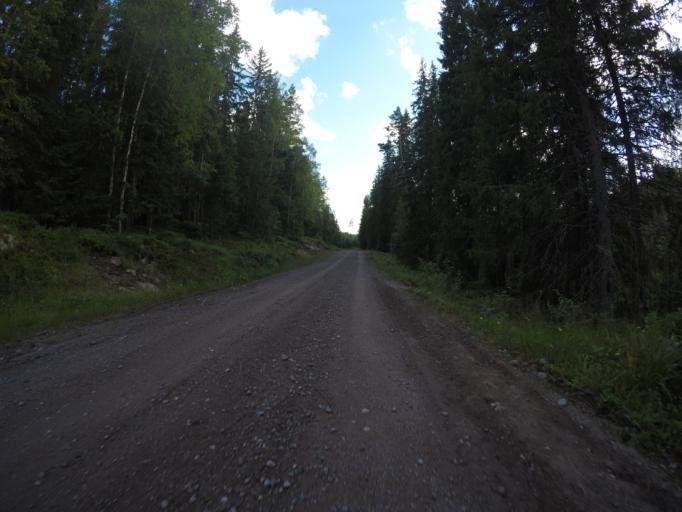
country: SE
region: Dalarna
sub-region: Ludvika Kommun
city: Abborrberget
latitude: 60.0066
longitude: 14.6091
